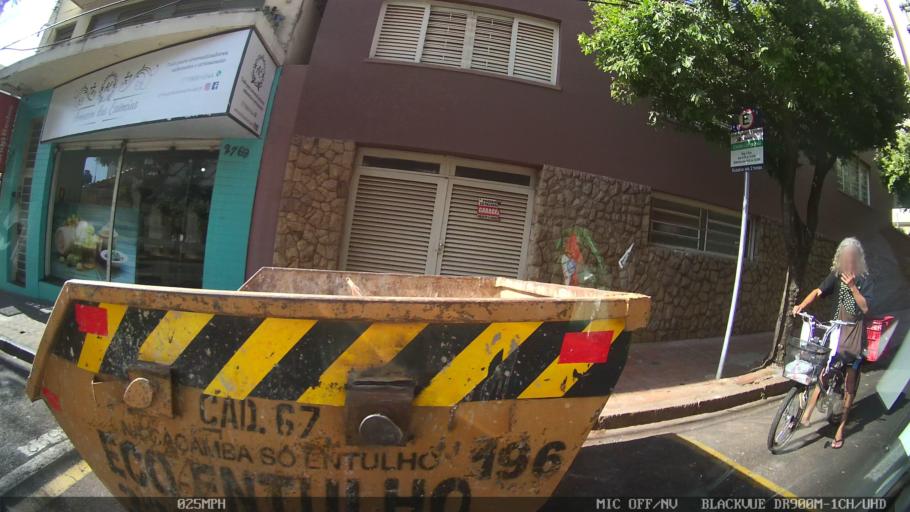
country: BR
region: Sao Paulo
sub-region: Sao Jose Do Rio Preto
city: Sao Jose do Rio Preto
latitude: -20.8139
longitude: -49.3862
